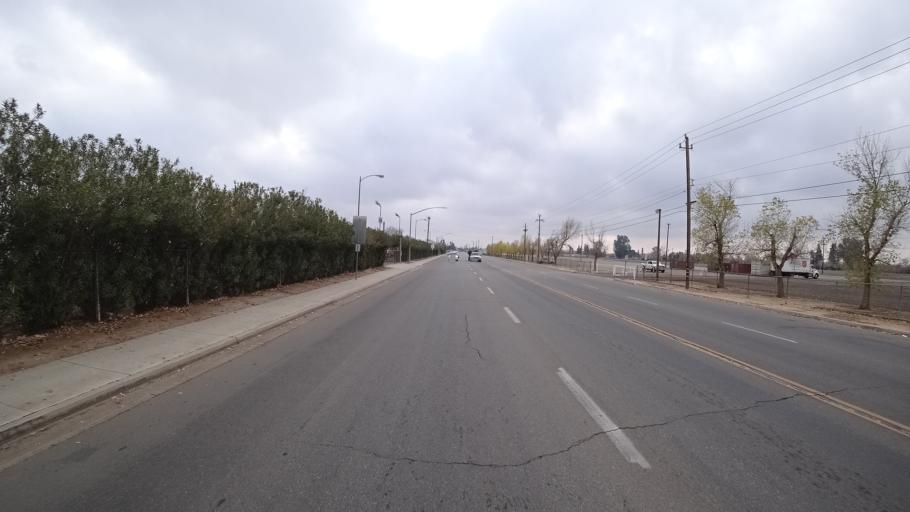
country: US
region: California
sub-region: Kern County
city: Bakersfield
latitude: 35.3462
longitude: -119.0118
